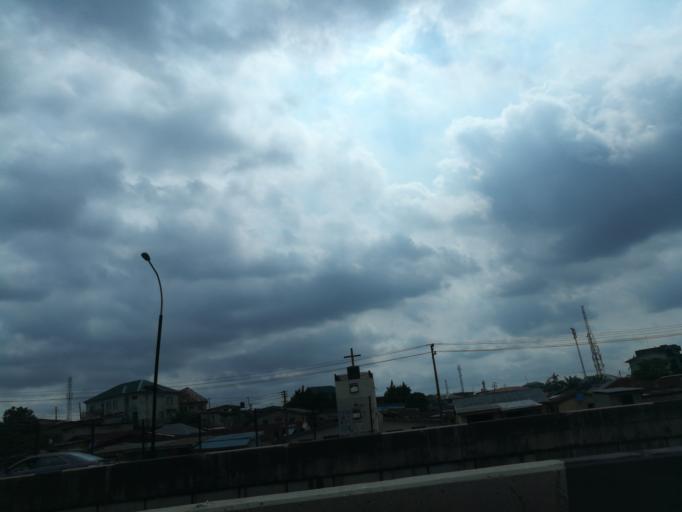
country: NG
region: Lagos
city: Somolu
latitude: 6.5562
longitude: 3.3966
